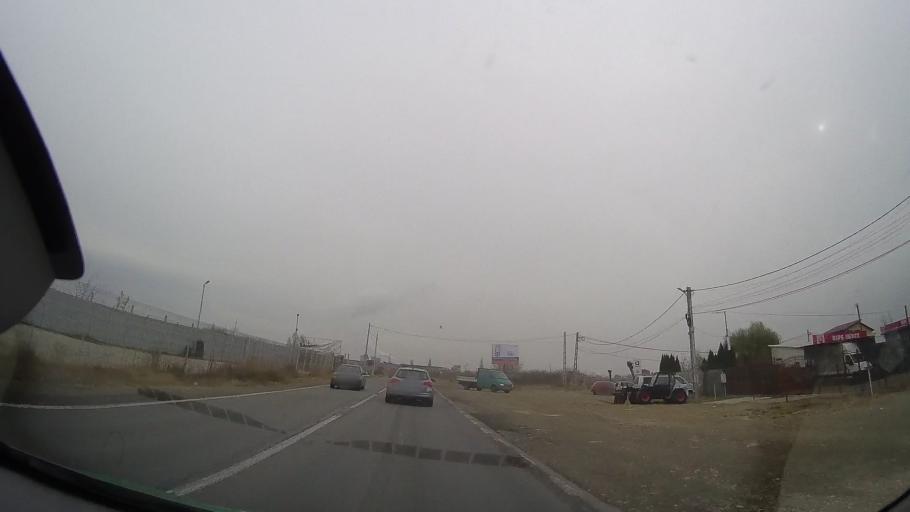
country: RO
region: Prahova
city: Ploiesti
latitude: 44.9605
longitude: 26.0440
